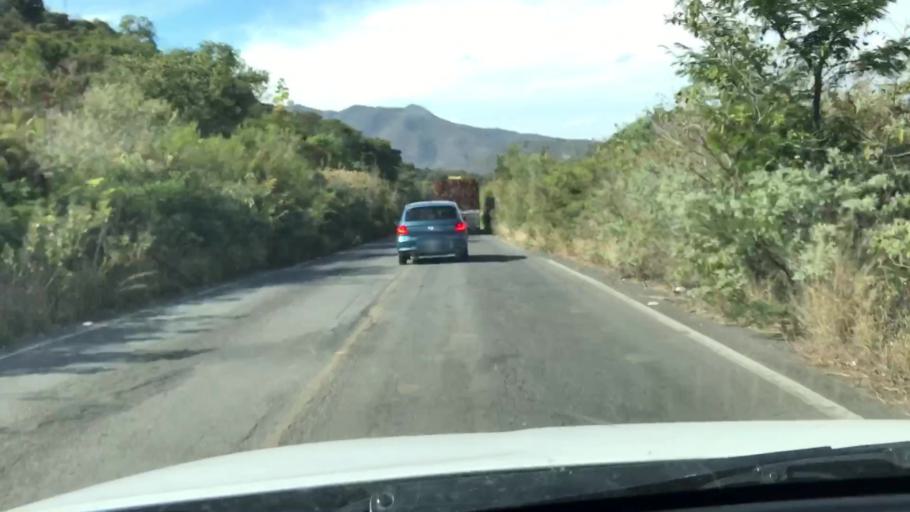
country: MX
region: Jalisco
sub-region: Zacoalco de Torres
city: Barranca de Otates (Barranca de Otatan)
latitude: 20.2284
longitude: -103.6792
